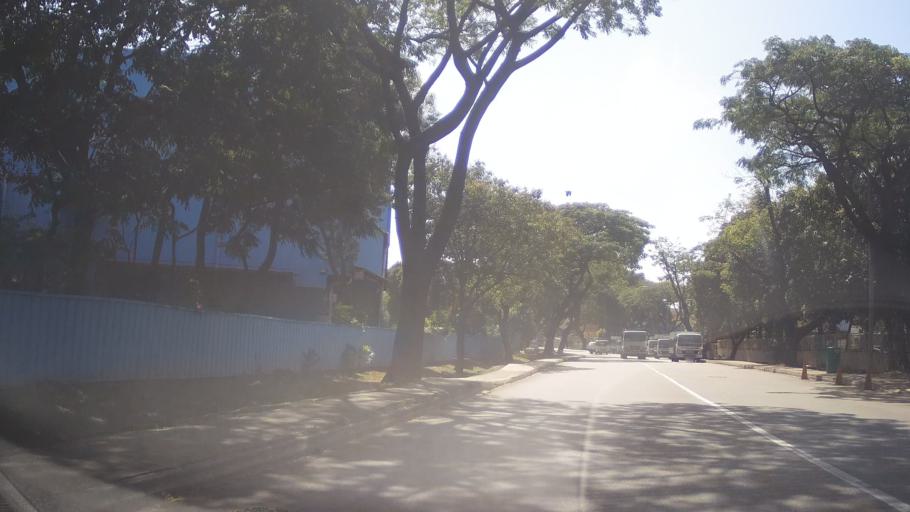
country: SG
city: Singapore
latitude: 1.3056
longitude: 103.7014
